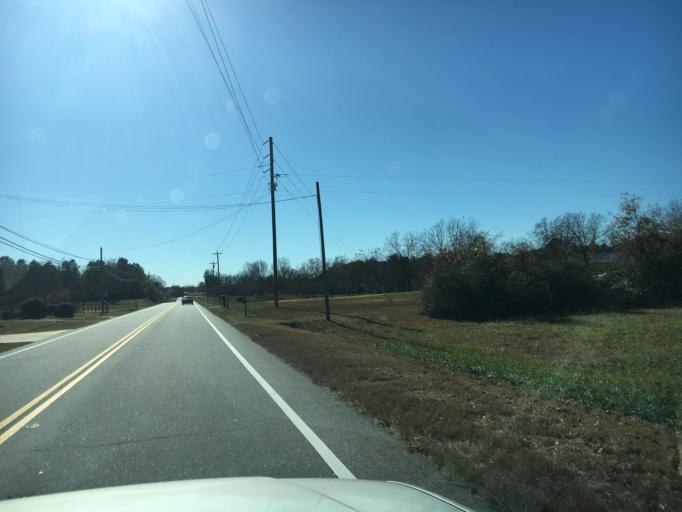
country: US
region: Georgia
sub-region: Hart County
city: Hartwell
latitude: 34.3004
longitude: -83.0041
